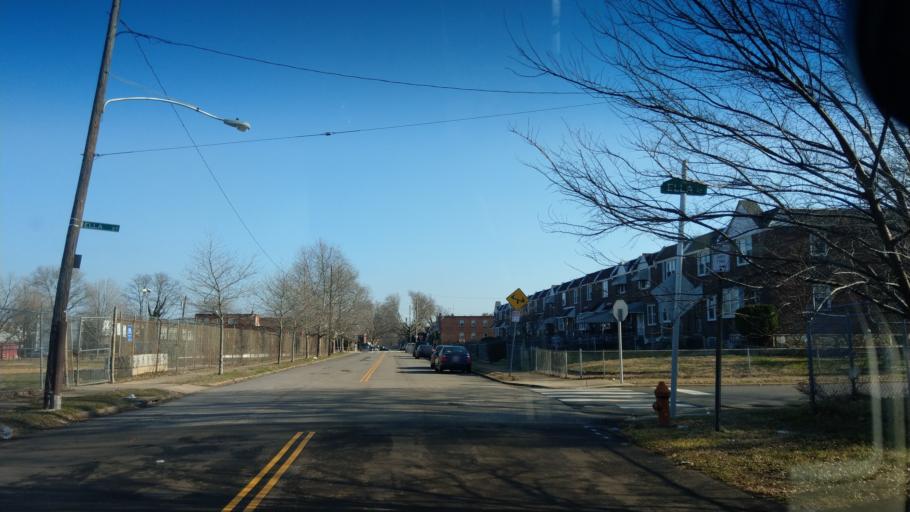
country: US
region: Pennsylvania
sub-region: Montgomery County
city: Rockledge
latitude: 40.0334
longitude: -75.1195
